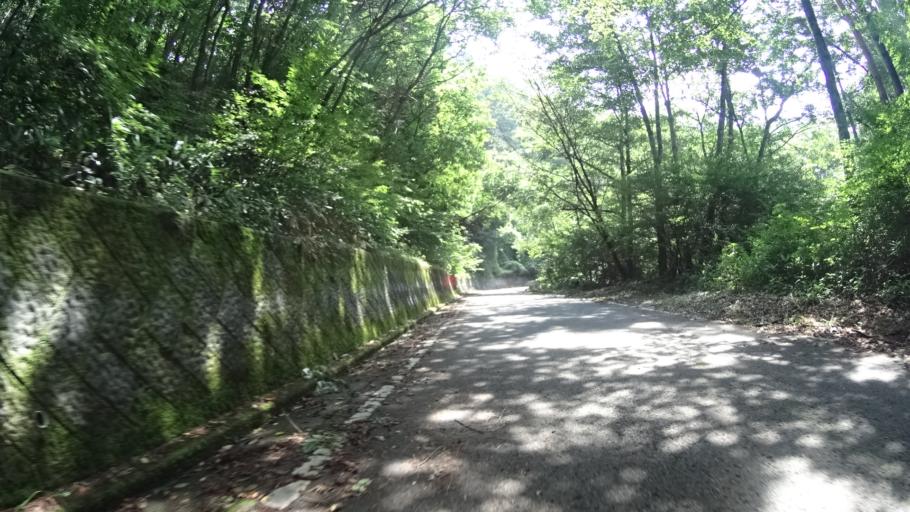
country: JP
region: Yamanashi
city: Nirasaki
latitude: 35.8871
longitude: 138.4768
